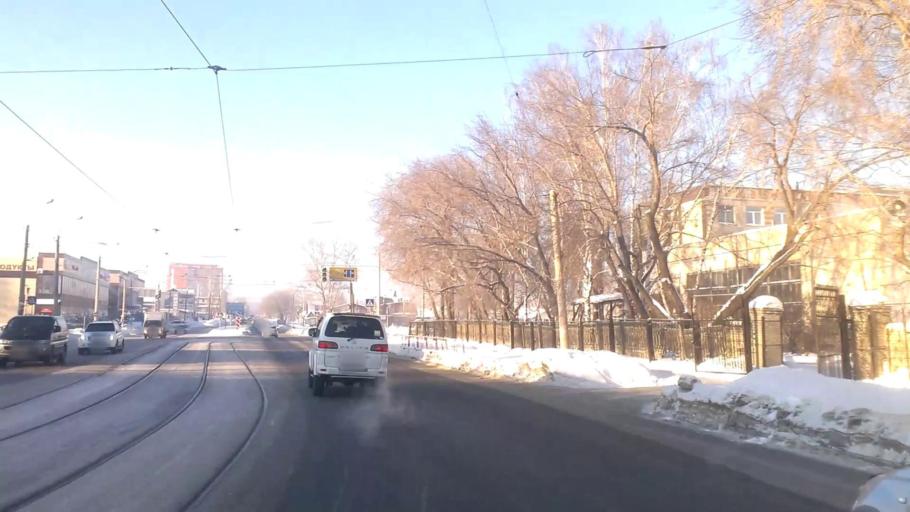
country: RU
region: Altai Krai
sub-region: Gorod Barnaulskiy
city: Barnaul
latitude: 53.3488
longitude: 83.7293
